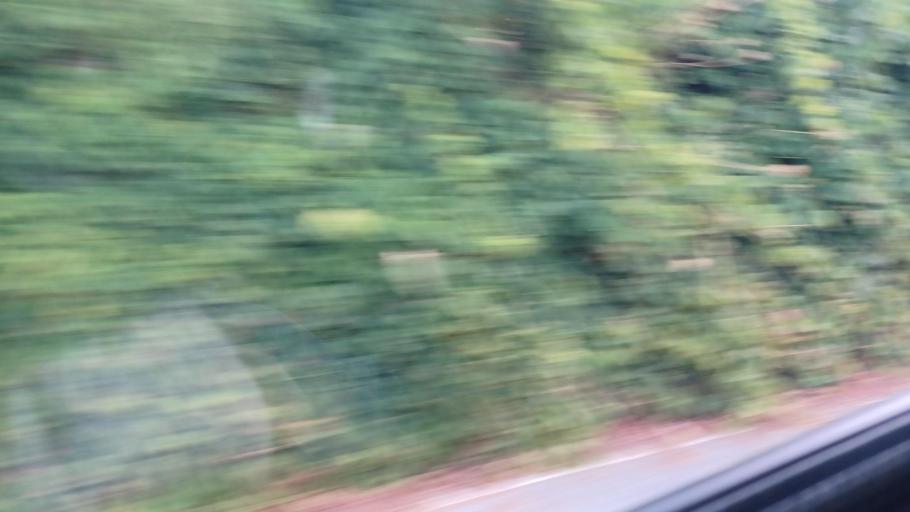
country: CY
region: Pafos
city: Mesogi
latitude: 34.8308
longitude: 32.5695
